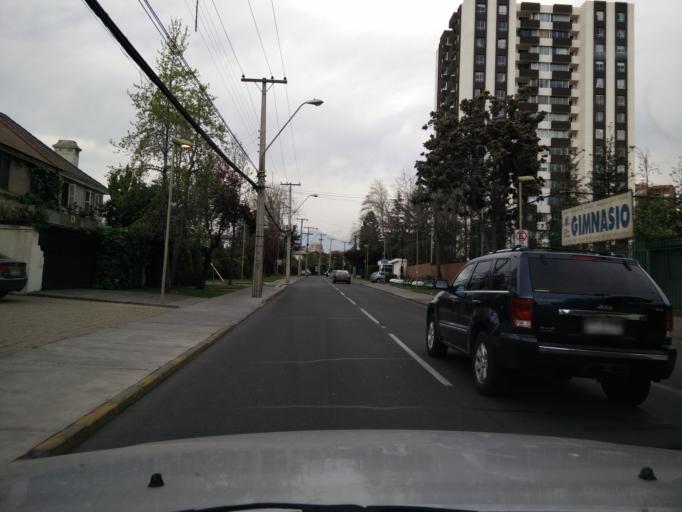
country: CL
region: Santiago Metropolitan
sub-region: Provincia de Santiago
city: Villa Presidente Frei, Nunoa, Santiago, Chile
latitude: -33.4197
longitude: -70.5779
